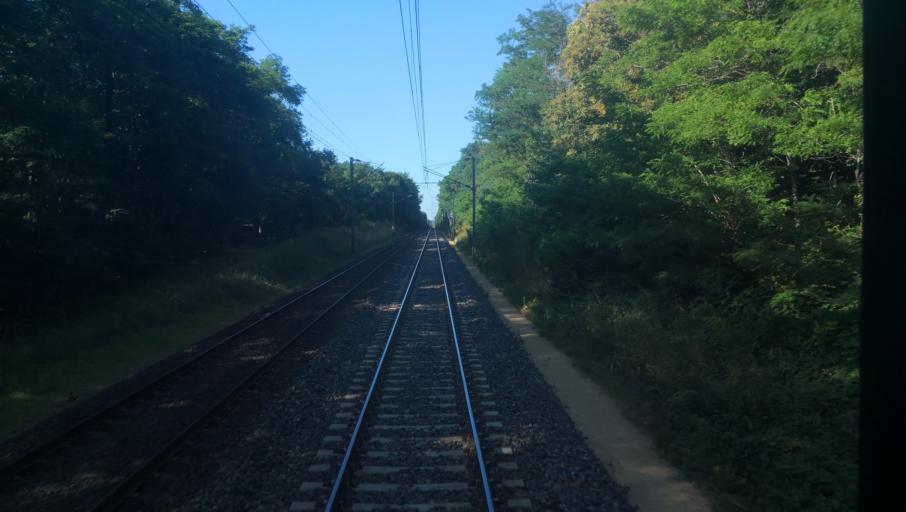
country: FR
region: Centre
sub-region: Departement du Cher
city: Saint-Satur
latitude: 47.3514
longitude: 2.8856
